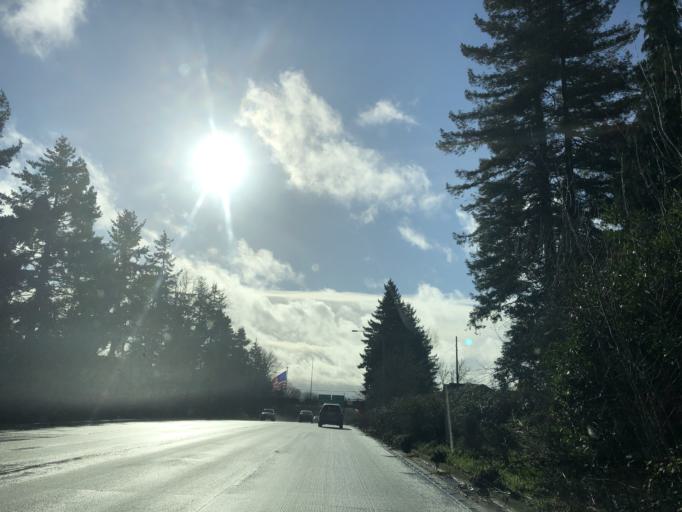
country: US
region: Washington
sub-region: Pierce County
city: Tacoma
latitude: 47.2385
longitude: -122.4633
